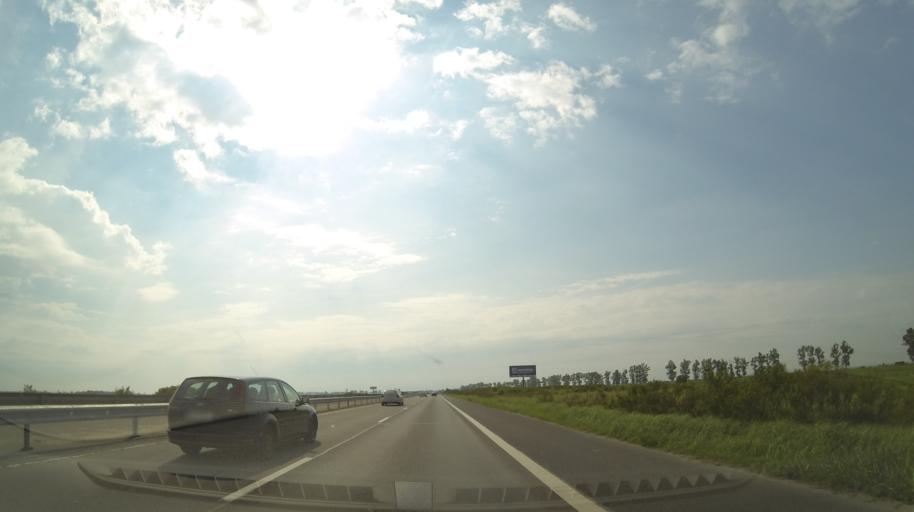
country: RO
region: Dambovita
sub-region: Comuna Corbii Mari
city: Corbii Mari
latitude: 44.5410
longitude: 25.5181
